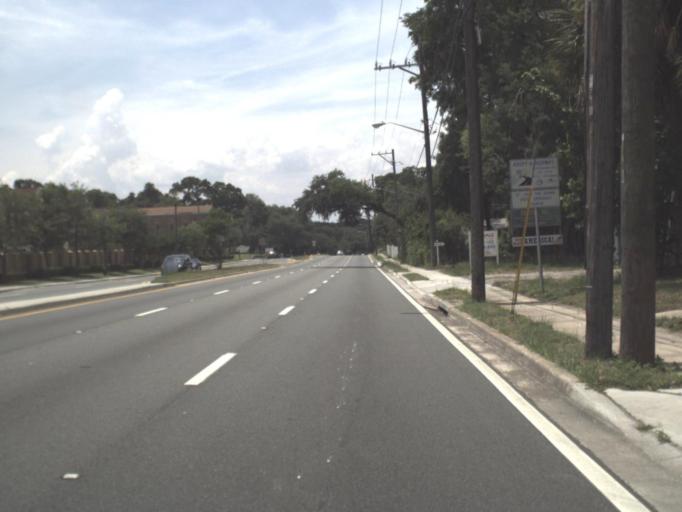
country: US
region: Florida
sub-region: Duval County
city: Jacksonville
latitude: 30.3129
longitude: -81.6033
